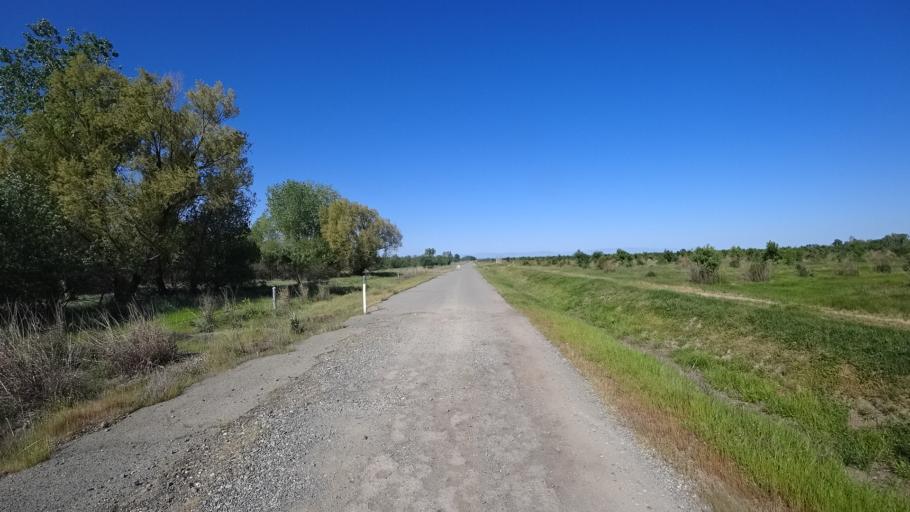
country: US
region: California
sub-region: Glenn County
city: Hamilton City
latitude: 39.7128
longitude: -121.9594
